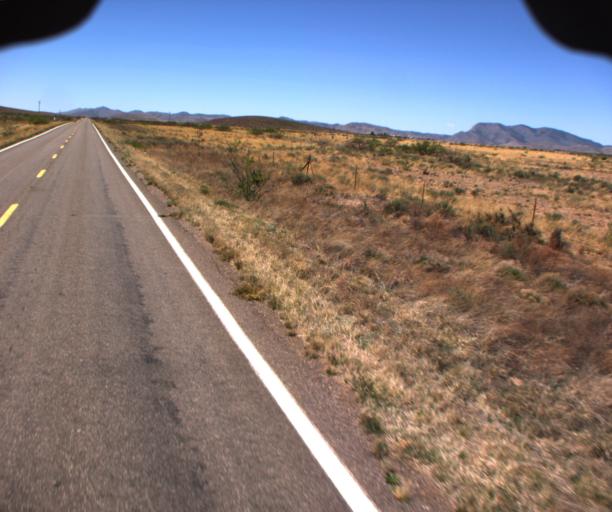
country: US
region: Arizona
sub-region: Cochise County
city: Douglas
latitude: 31.6395
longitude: -109.1798
